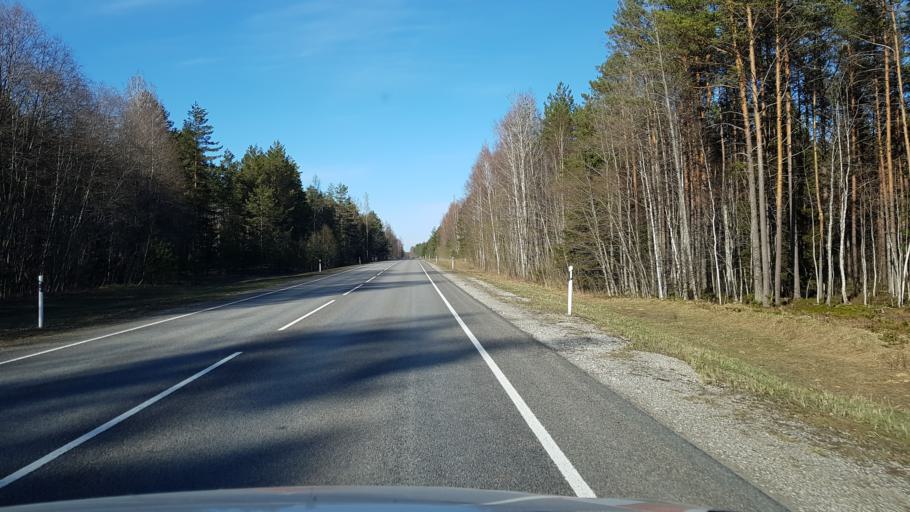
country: EE
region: Ida-Virumaa
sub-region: Kohtla-Nomme vald
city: Kohtla-Nomme
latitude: 59.0282
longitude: 27.2330
